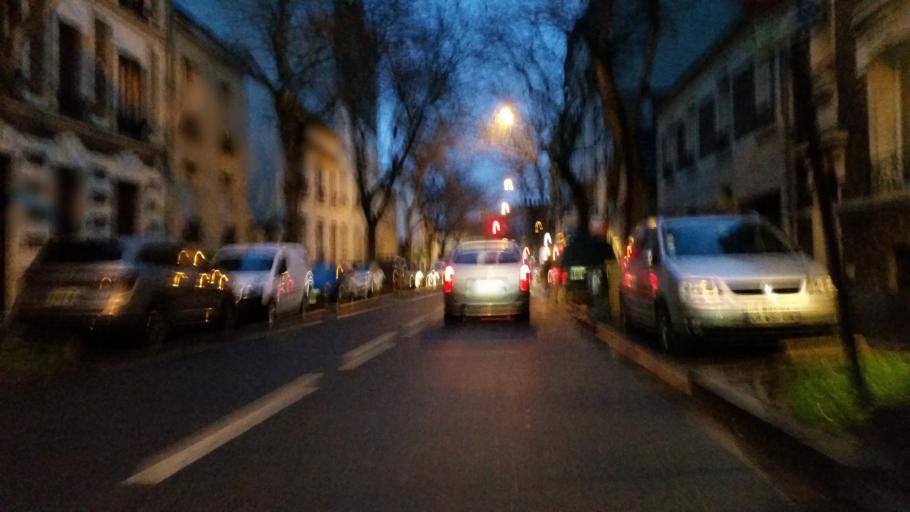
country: FR
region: Ile-de-France
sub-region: Departement du Val-de-Marne
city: Vitry-sur-Seine
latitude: 48.8003
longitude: 2.4000
